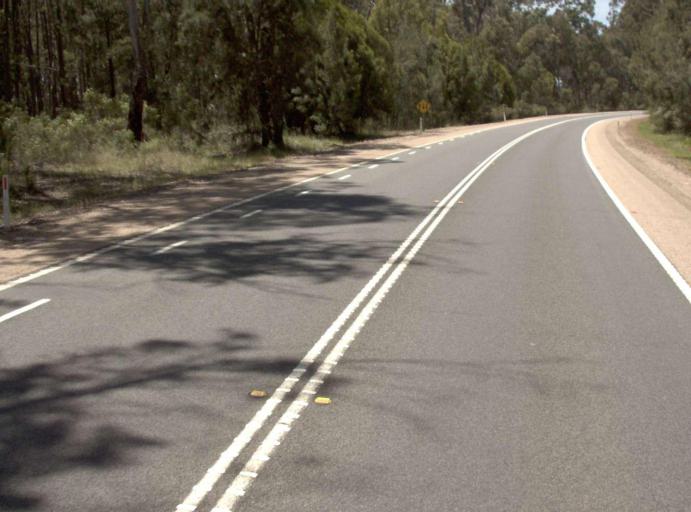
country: AU
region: Victoria
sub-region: East Gippsland
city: Bairnsdale
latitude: -37.7369
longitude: 147.7694
